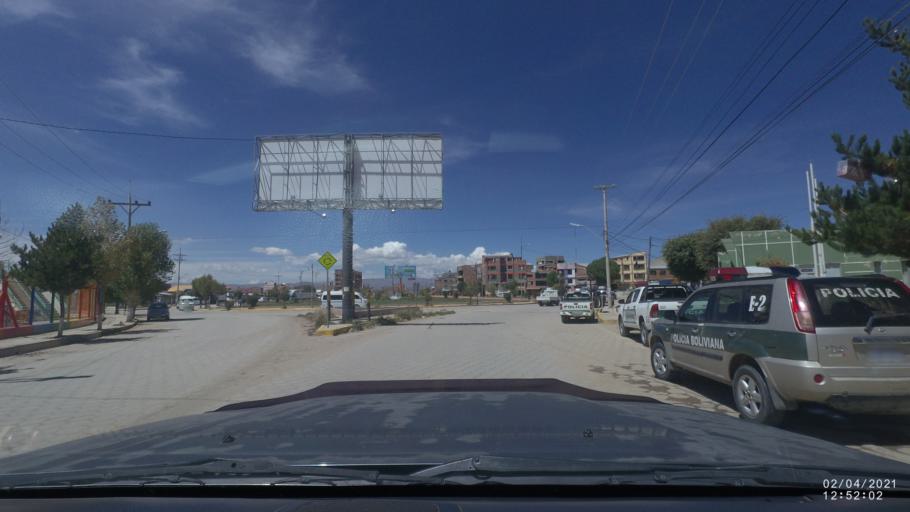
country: BO
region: Oruro
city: Oruro
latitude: -17.9861
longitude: -67.1348
